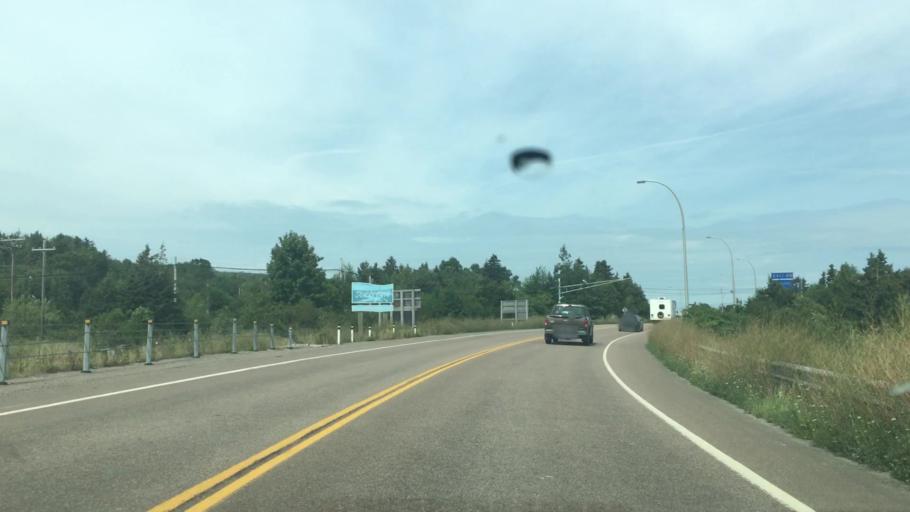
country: CA
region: Nova Scotia
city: Port Hawkesbury
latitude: 45.6452
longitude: -61.4347
